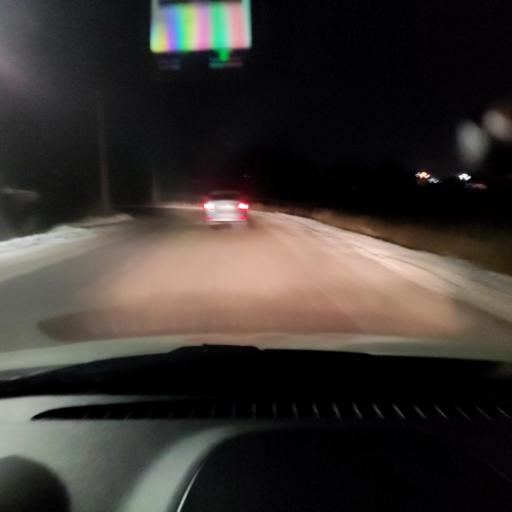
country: RU
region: Tatarstan
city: Vysokaya Gora
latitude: 55.8072
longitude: 49.3783
